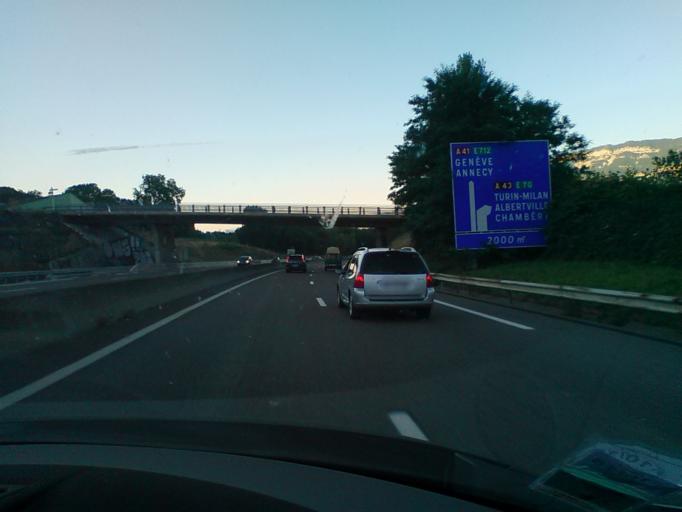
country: FR
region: Rhone-Alpes
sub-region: Departement de la Savoie
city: La Motte-Servolex
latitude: 45.6009
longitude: 5.8569
